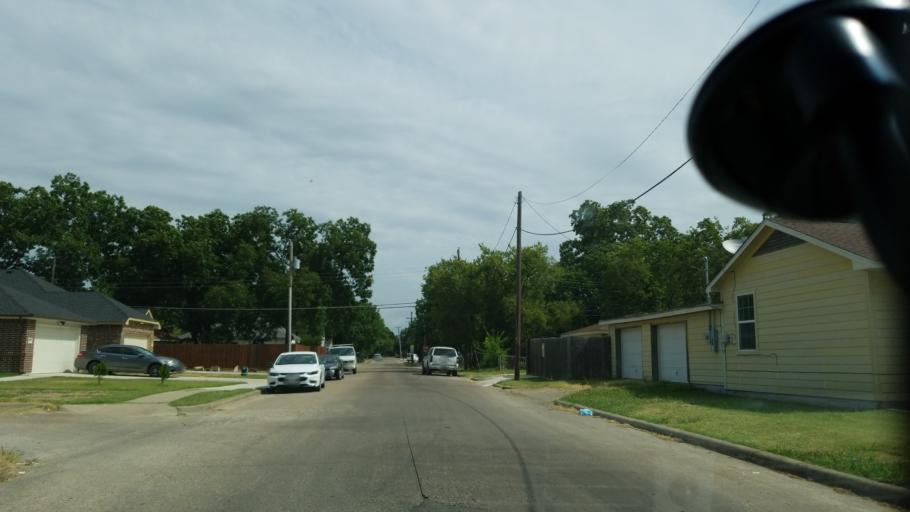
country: US
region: Texas
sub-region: Dallas County
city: Grand Prairie
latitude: 32.7498
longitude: -96.9887
